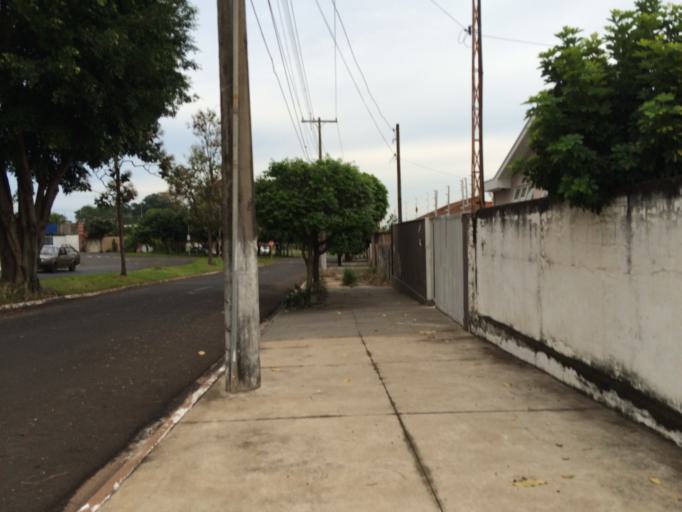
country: BR
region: Sao Paulo
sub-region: Matao
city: Matao
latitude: -21.6142
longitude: -48.3656
